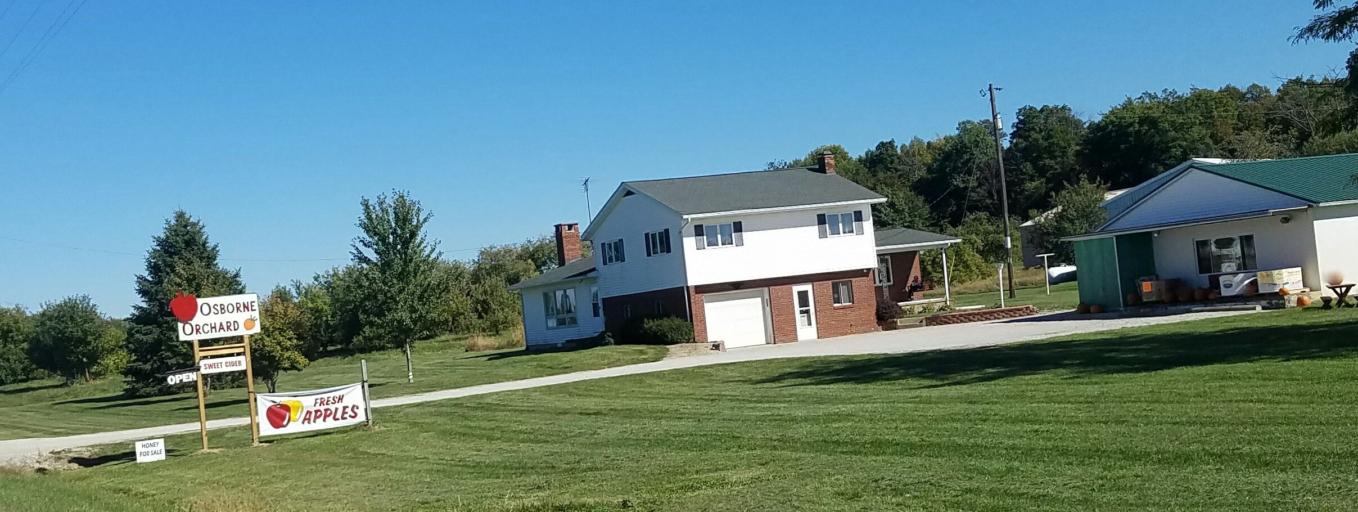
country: US
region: Ohio
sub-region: Morrow County
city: Mount Gilead
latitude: 40.5735
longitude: -82.7385
